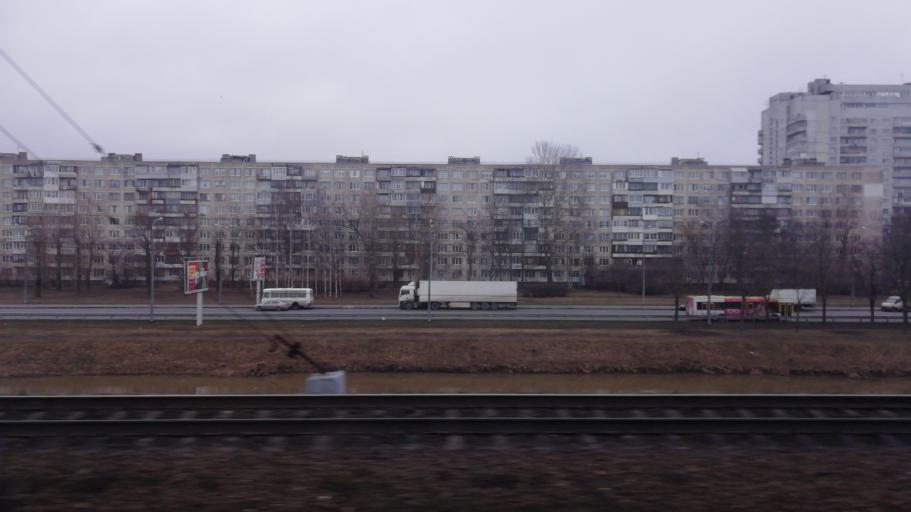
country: RU
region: St.-Petersburg
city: Kupchino
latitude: 59.8703
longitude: 30.3563
